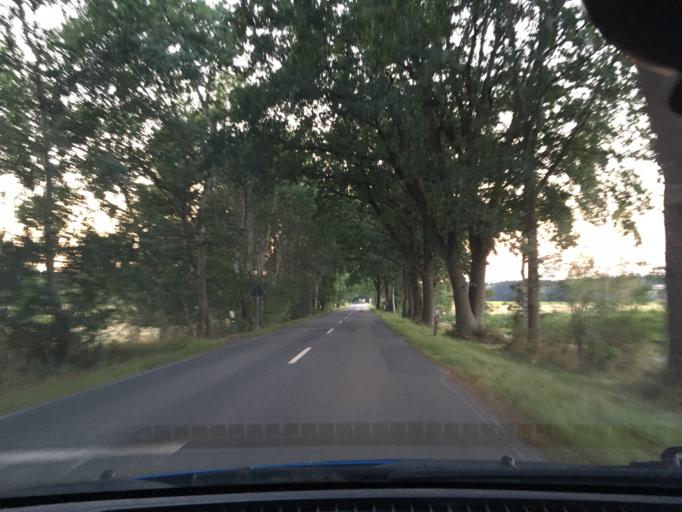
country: DE
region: Lower Saxony
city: Barnstedt
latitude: 53.1463
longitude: 10.3627
